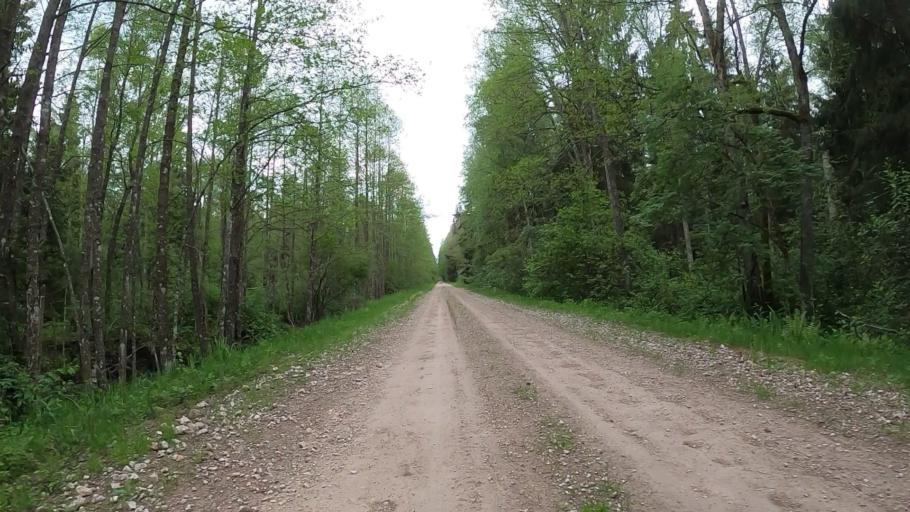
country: LV
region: Ozolnieku
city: Ozolnieki
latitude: 56.8064
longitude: 23.7861
